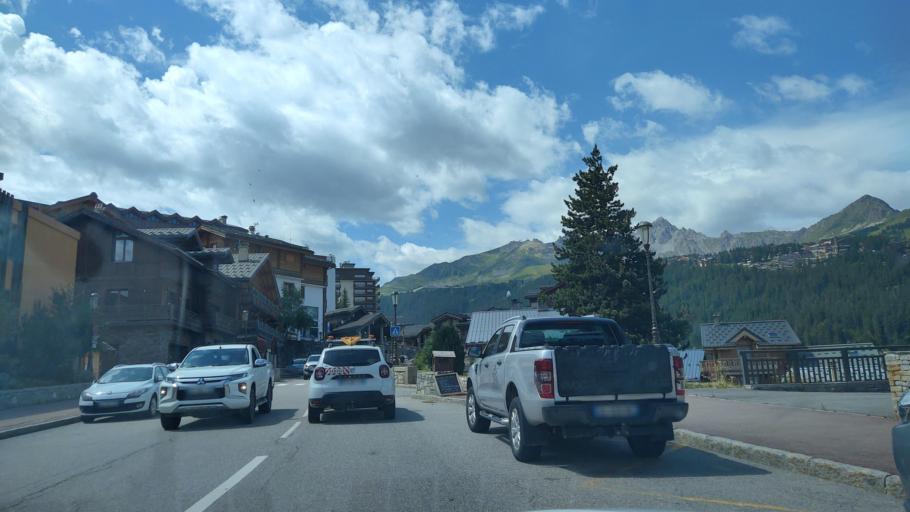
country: FR
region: Rhone-Alpes
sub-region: Departement de la Savoie
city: Courchevel
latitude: 45.4186
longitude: 6.6528
